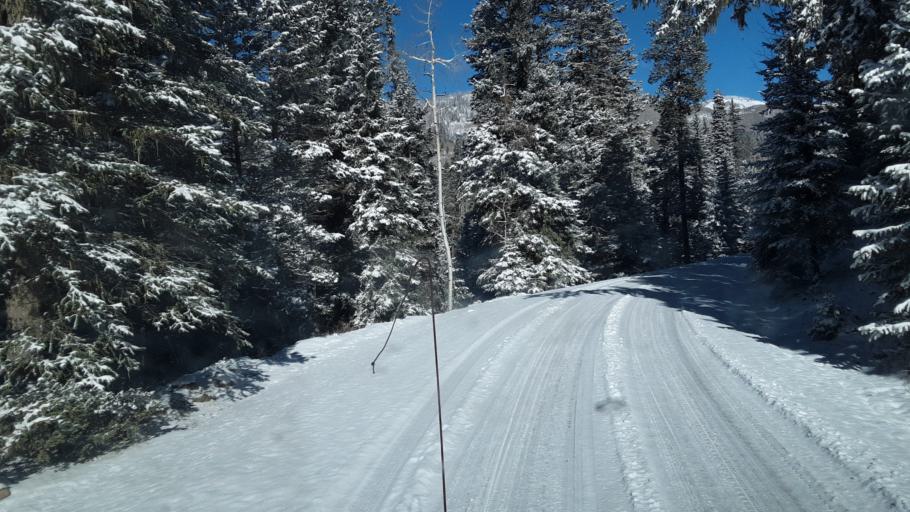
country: US
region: Colorado
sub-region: La Plata County
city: Bayfield
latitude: 37.4465
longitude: -107.6811
